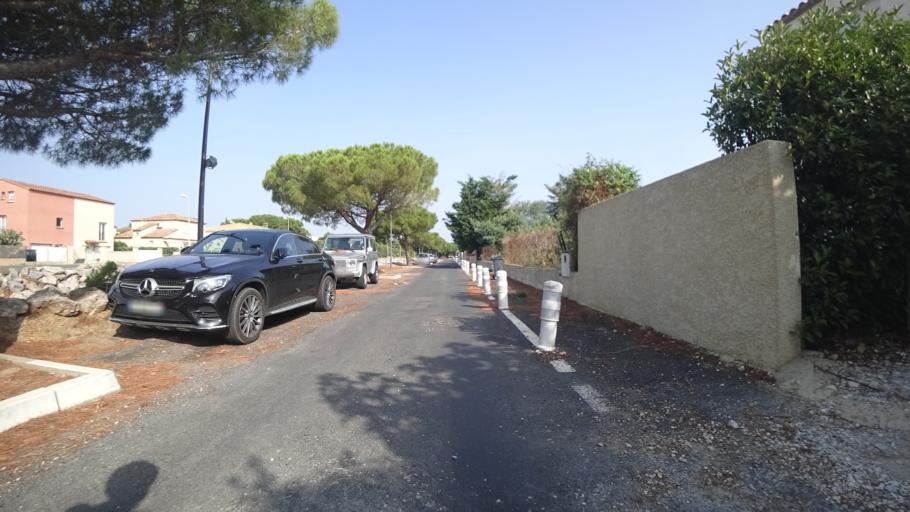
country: FR
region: Languedoc-Roussillon
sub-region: Departement des Pyrenees-Orientales
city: Sainte-Marie-Plage
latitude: 42.7270
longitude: 3.0311
